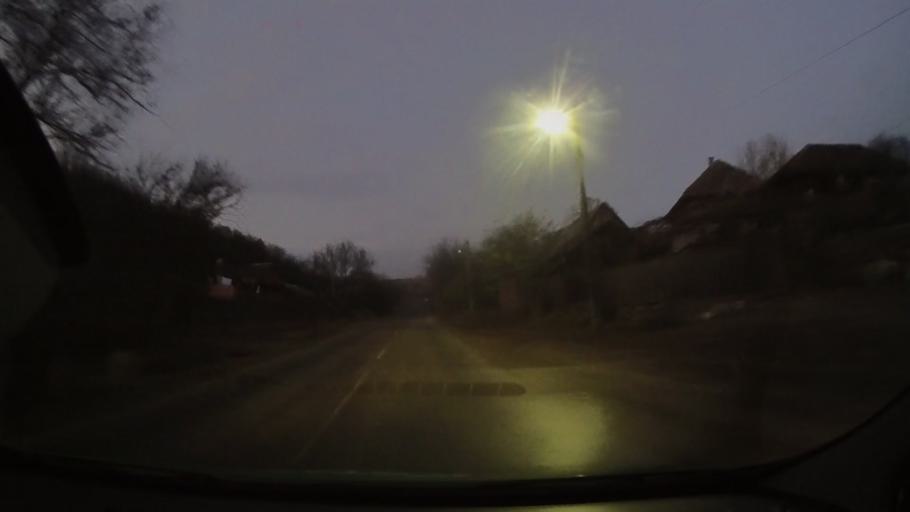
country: RO
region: Constanta
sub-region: Comuna Ion Corvin
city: Ion Corvin
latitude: 44.1163
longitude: 27.8108
